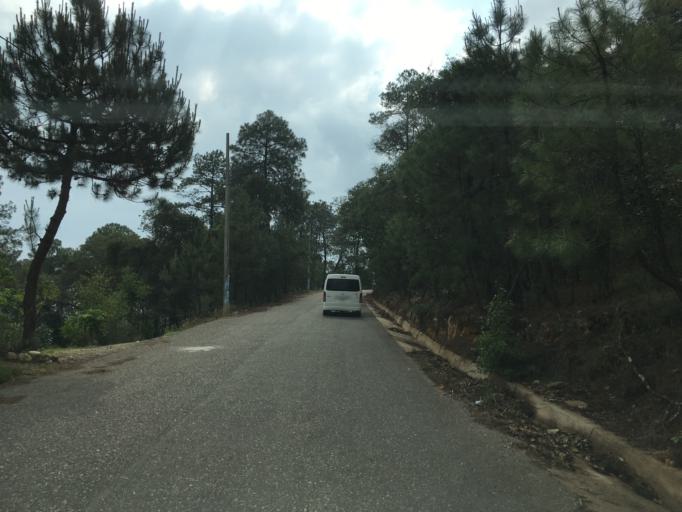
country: MX
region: Oaxaca
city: Santiago Tilantongo
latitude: 17.2106
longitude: -97.2803
